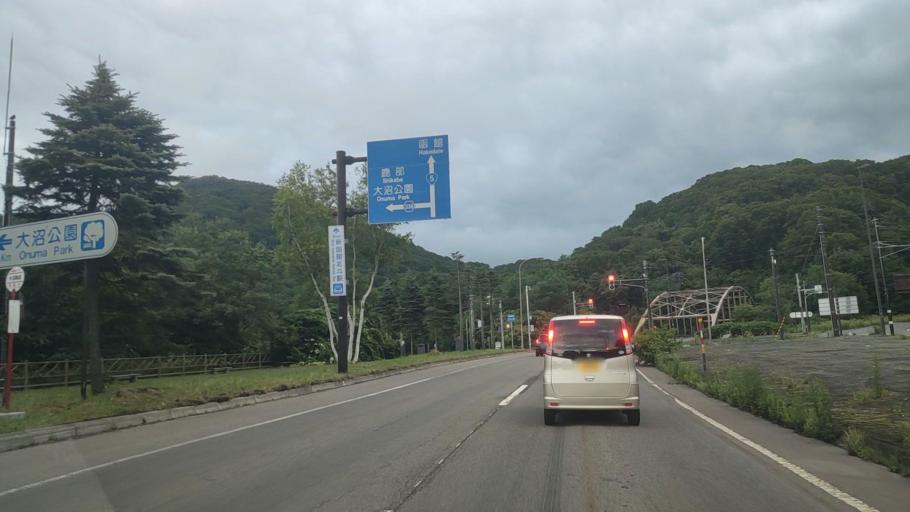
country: JP
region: Hokkaido
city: Nanae
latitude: 41.9571
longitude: 140.6503
